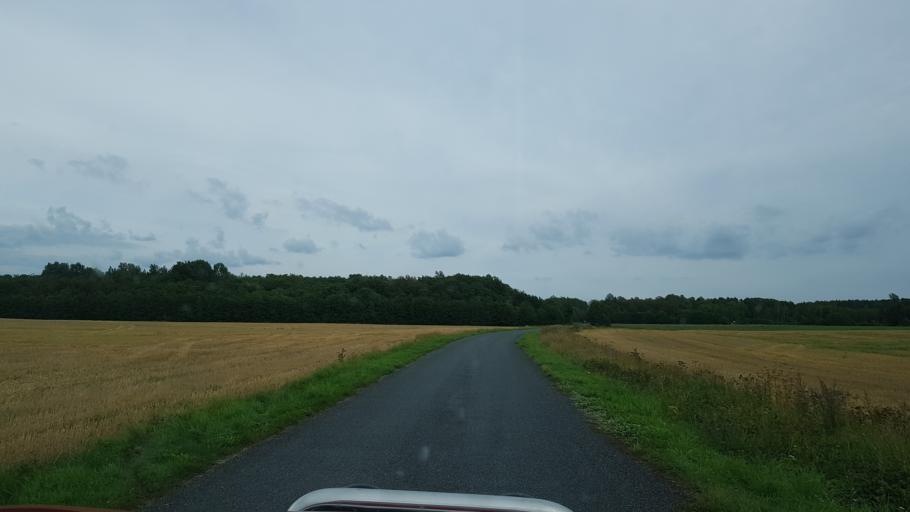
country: EE
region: Laeaene
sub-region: Ridala Parish
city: Uuemoisa
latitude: 58.9838
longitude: 23.8102
